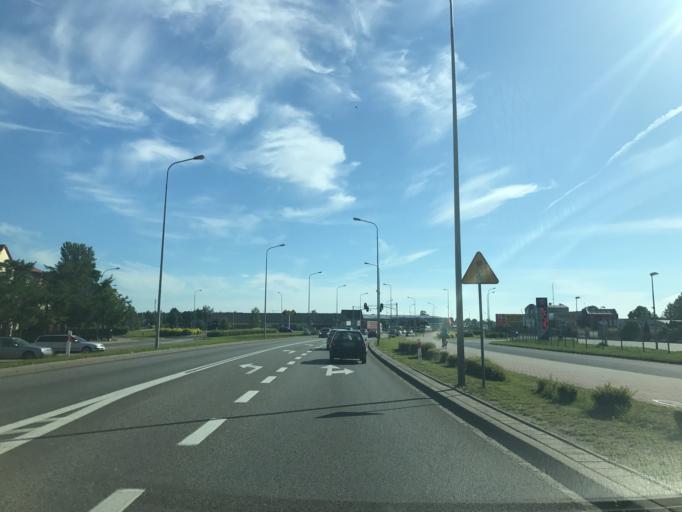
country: PL
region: Pomeranian Voivodeship
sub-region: Powiat czluchowski
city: Czluchow
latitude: 53.6721
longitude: 17.3574
